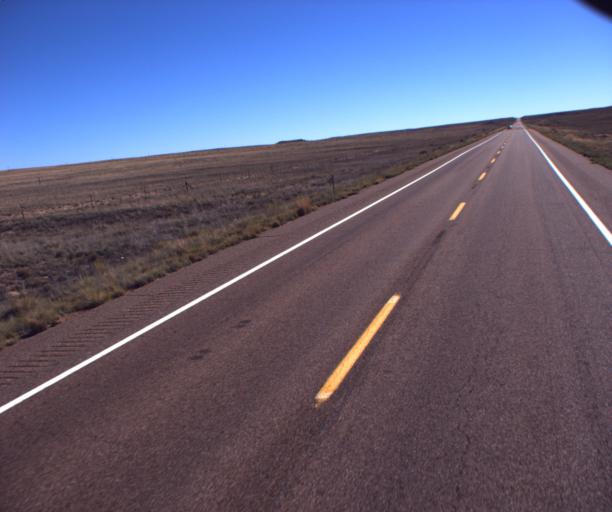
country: US
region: Arizona
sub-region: Navajo County
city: Holbrook
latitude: 34.7847
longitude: -109.8656
